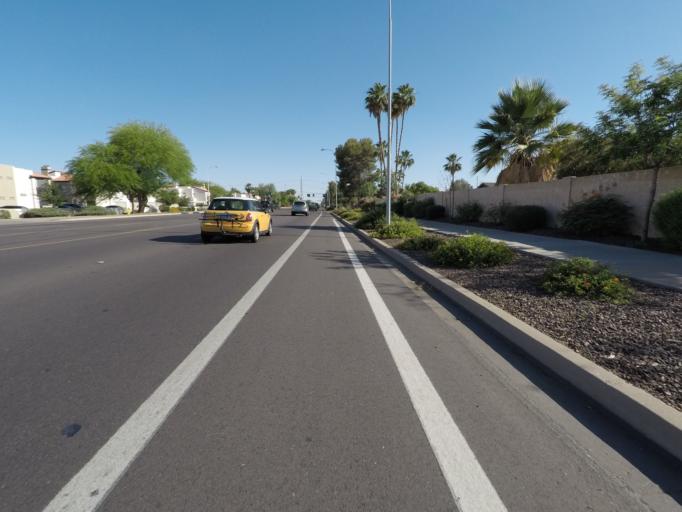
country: US
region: Arizona
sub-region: Maricopa County
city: Guadalupe
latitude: 33.3611
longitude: -111.9113
